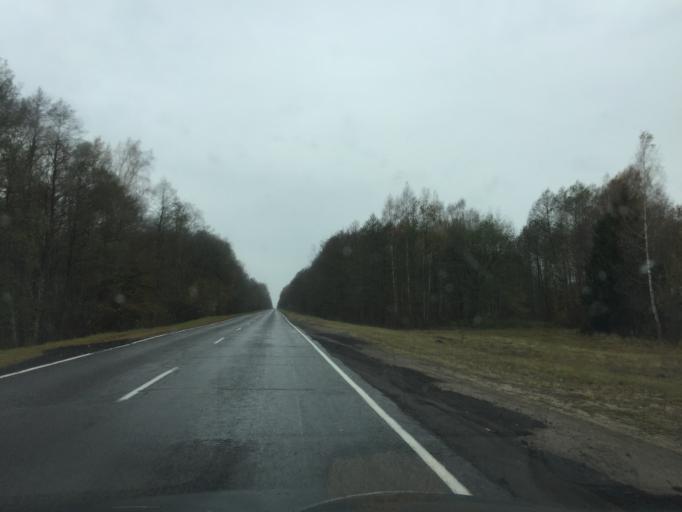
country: BY
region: Mogilev
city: Slawharad
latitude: 53.3752
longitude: 30.8712
